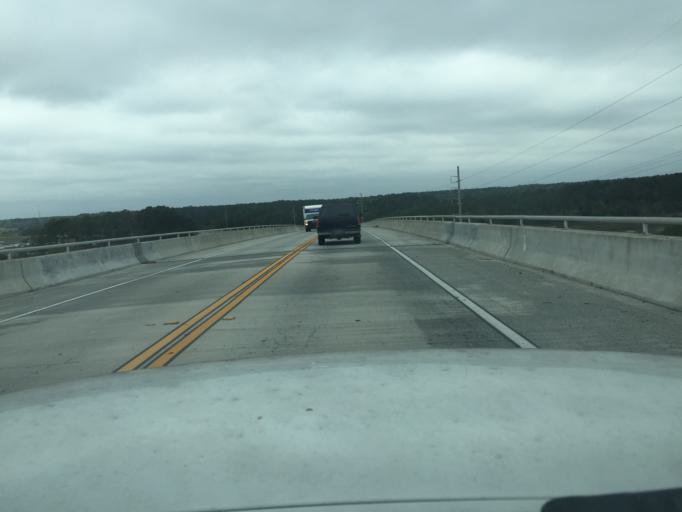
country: US
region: Georgia
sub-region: Chatham County
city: Skidaway Island
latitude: 31.9477
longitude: -81.0660
